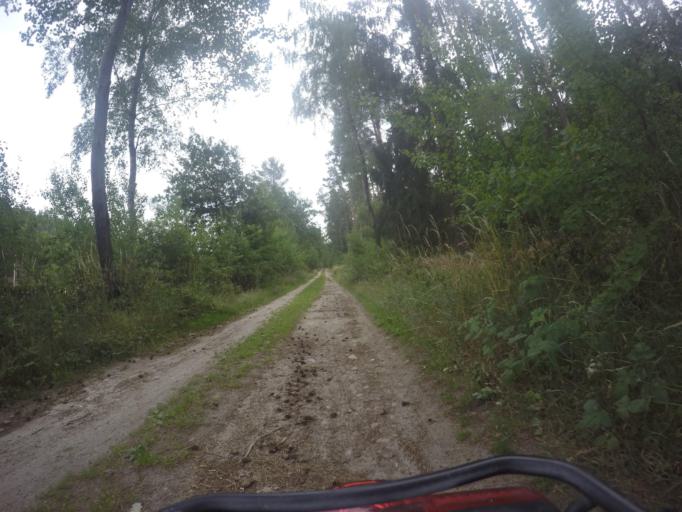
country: DE
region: Lower Saxony
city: Dahlem
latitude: 53.2188
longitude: 10.7346
